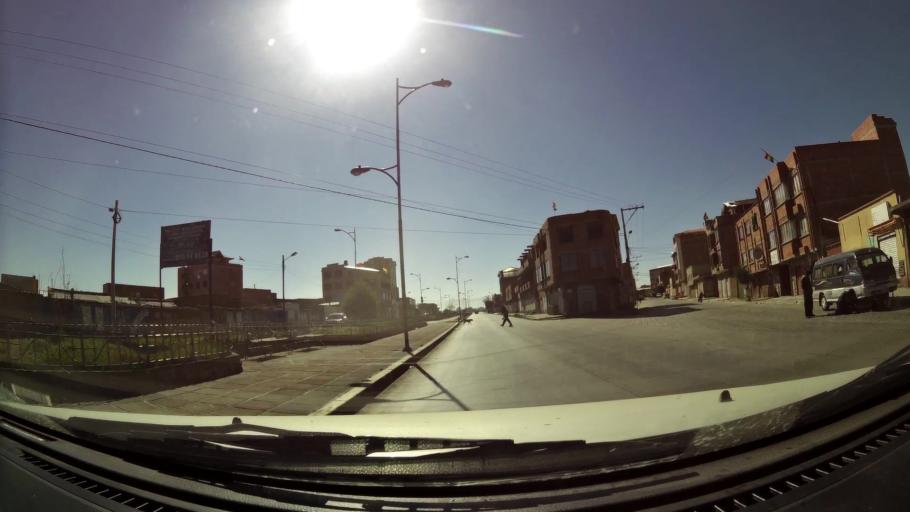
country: BO
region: La Paz
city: La Paz
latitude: -16.5174
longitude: -68.1826
